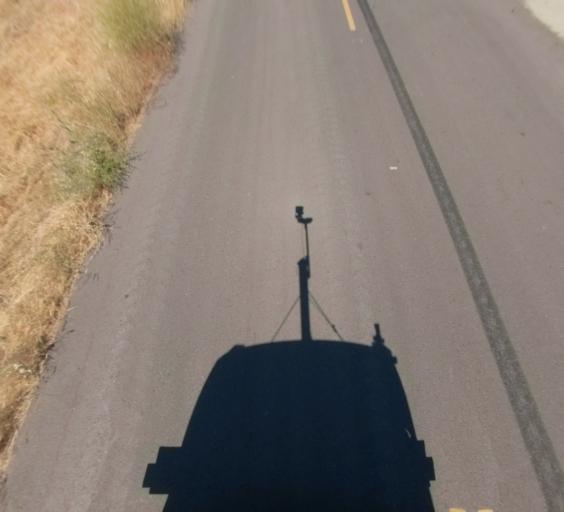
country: US
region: California
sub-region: Madera County
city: Bonadelle Ranchos-Madera Ranchos
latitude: 36.9885
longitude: -119.8692
